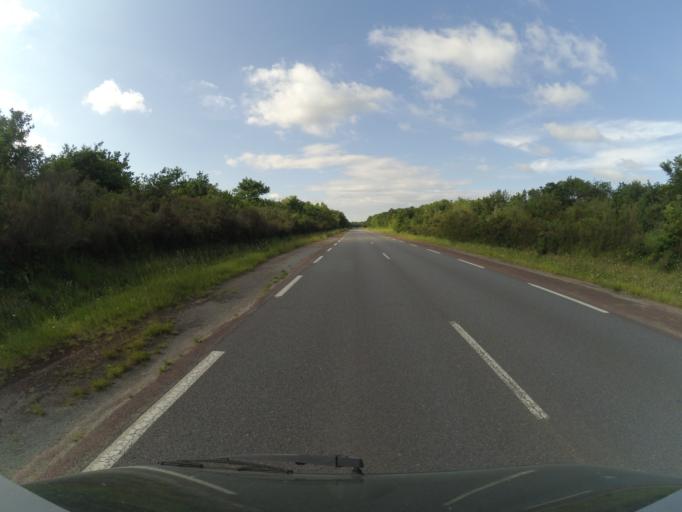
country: FR
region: Poitou-Charentes
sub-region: Departement de la Charente-Maritime
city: Le Gua
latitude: 45.7951
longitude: -0.9361
